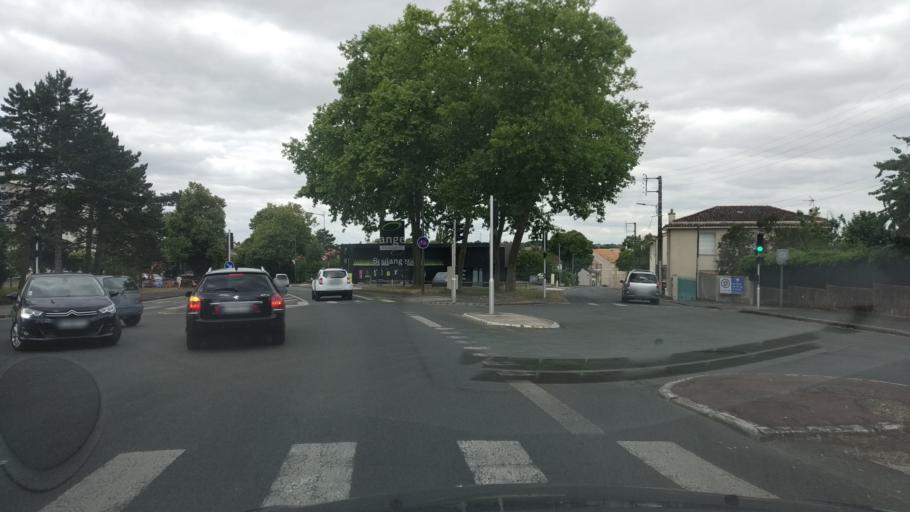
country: FR
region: Poitou-Charentes
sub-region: Departement de la Vienne
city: Poitiers
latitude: 46.5919
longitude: 0.3507
